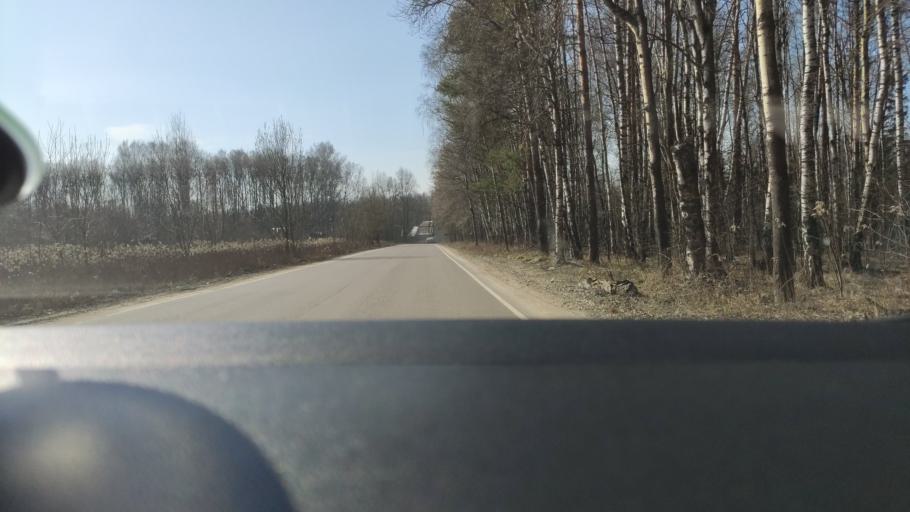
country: RU
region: Moskovskaya
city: Elektrostal'
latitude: 55.7669
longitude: 38.4030
